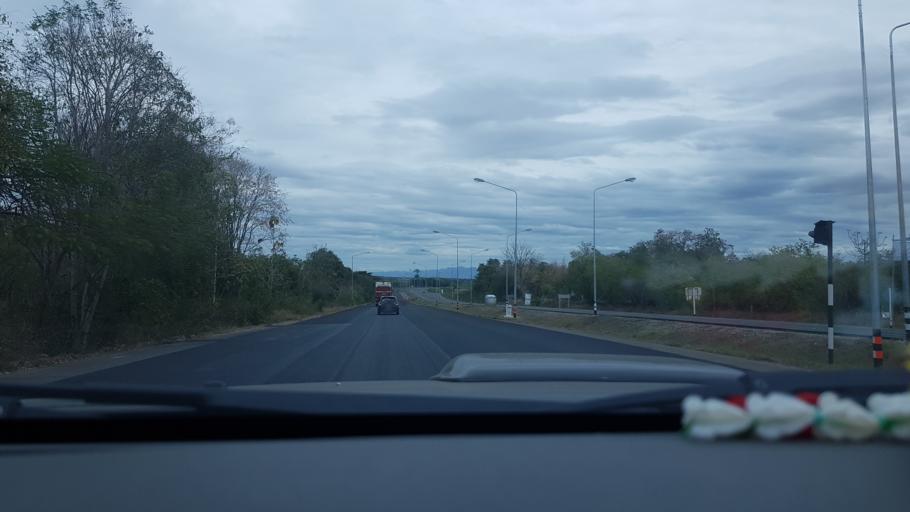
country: TH
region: Phetchabun
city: Phetchabun
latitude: 16.4873
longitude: 101.1393
